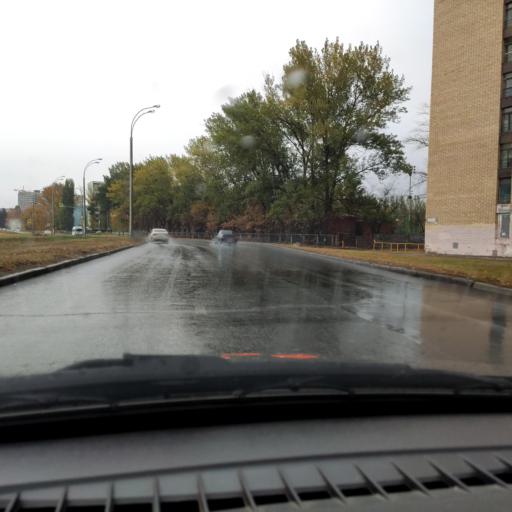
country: RU
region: Samara
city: Tol'yatti
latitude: 53.5290
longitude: 49.2785
